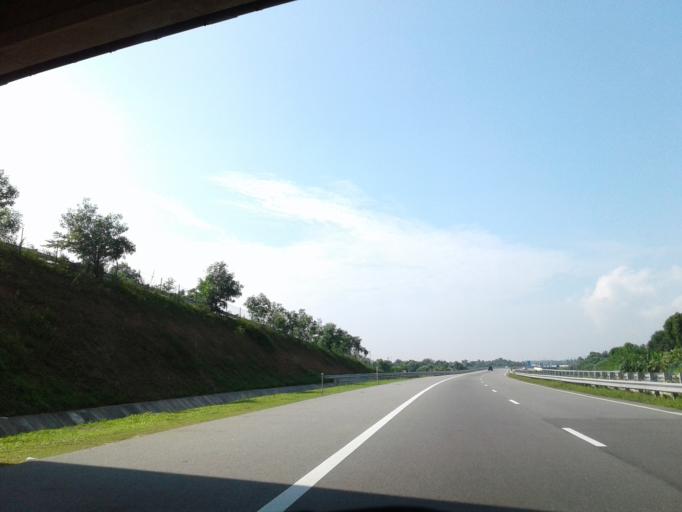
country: LK
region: Western
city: Mulleriyawa
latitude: 6.9505
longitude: 79.9762
